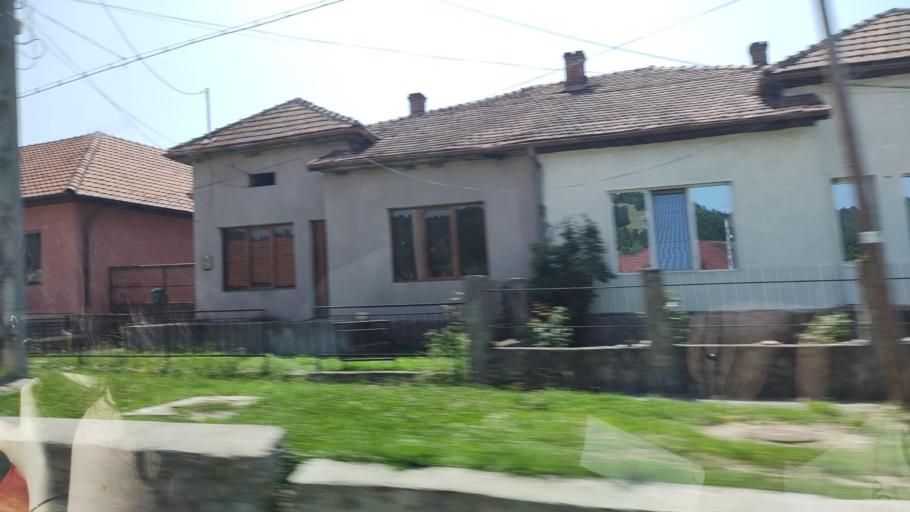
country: RO
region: Mehedinti
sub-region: Comuna Eselnita
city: Eselnita
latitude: 44.7038
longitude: 22.3611
